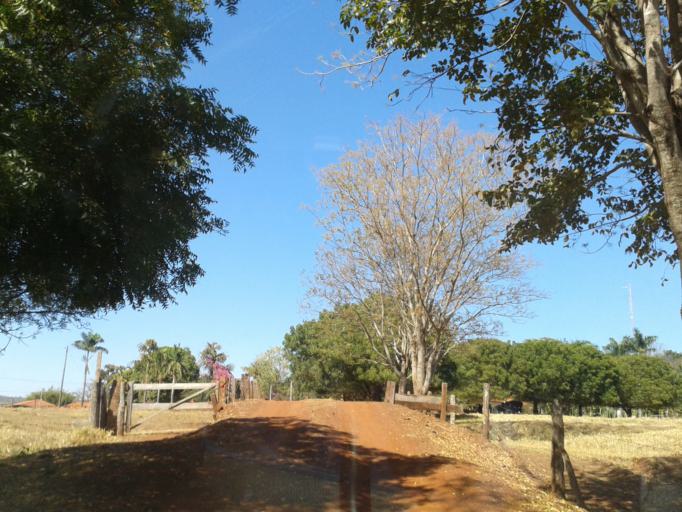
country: BR
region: Minas Gerais
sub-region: Santa Vitoria
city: Santa Vitoria
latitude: -19.1045
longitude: -49.9810
